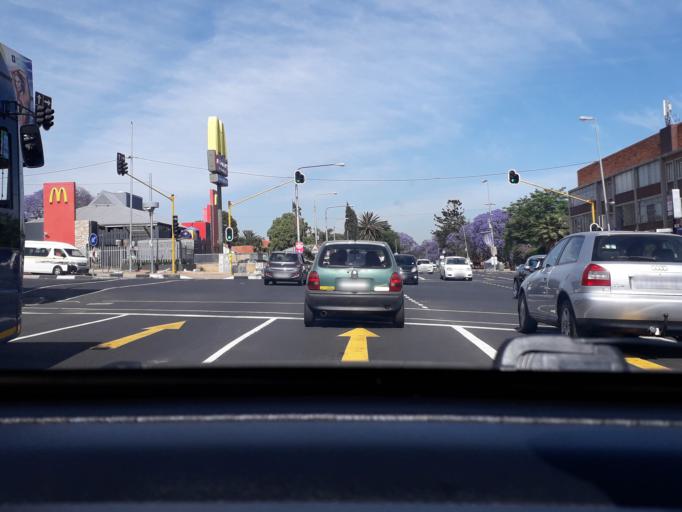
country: ZA
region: Gauteng
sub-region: City of Johannesburg Metropolitan Municipality
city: Johannesburg
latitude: -26.1396
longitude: 28.0870
